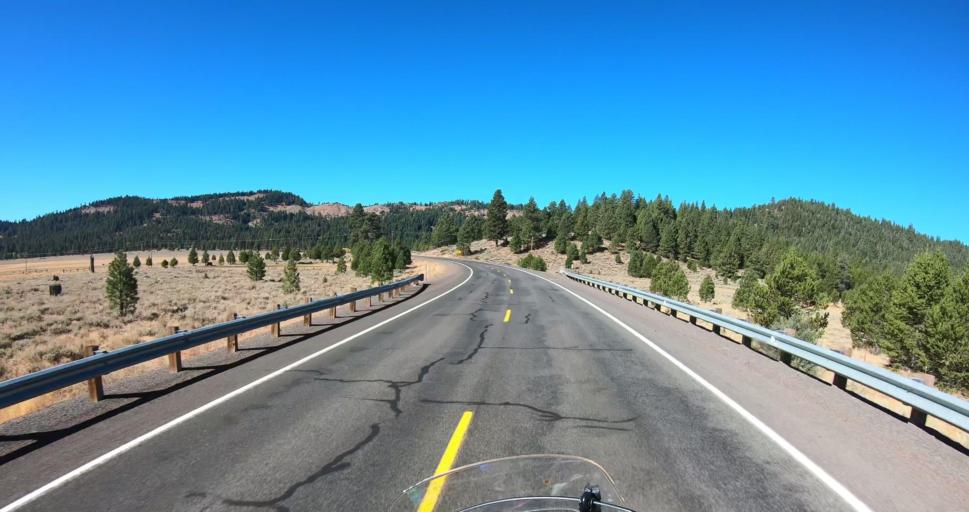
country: US
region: Oregon
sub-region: Lake County
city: Lakeview
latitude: 42.2294
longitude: -120.2742
